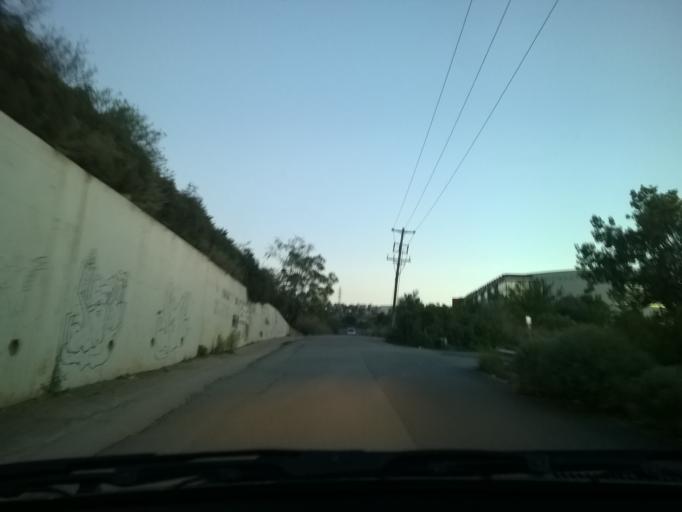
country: GR
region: Central Macedonia
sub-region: Nomos Thessalonikis
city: Polichni
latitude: 40.6714
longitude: 22.9609
